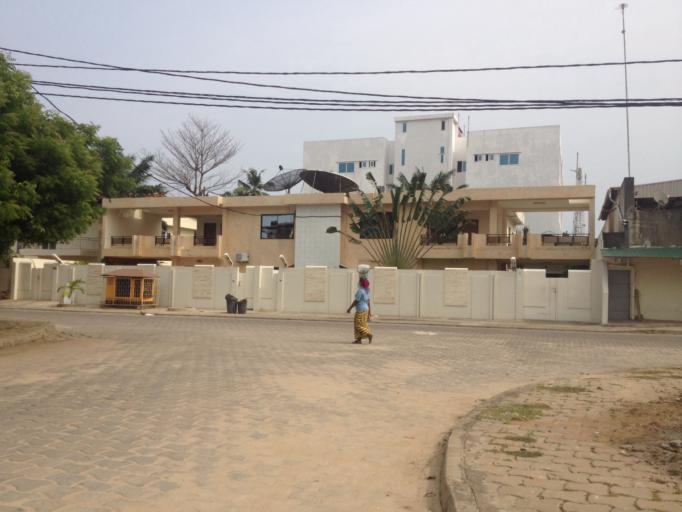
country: BJ
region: Littoral
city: Cotonou
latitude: 6.3549
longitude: 2.4051
